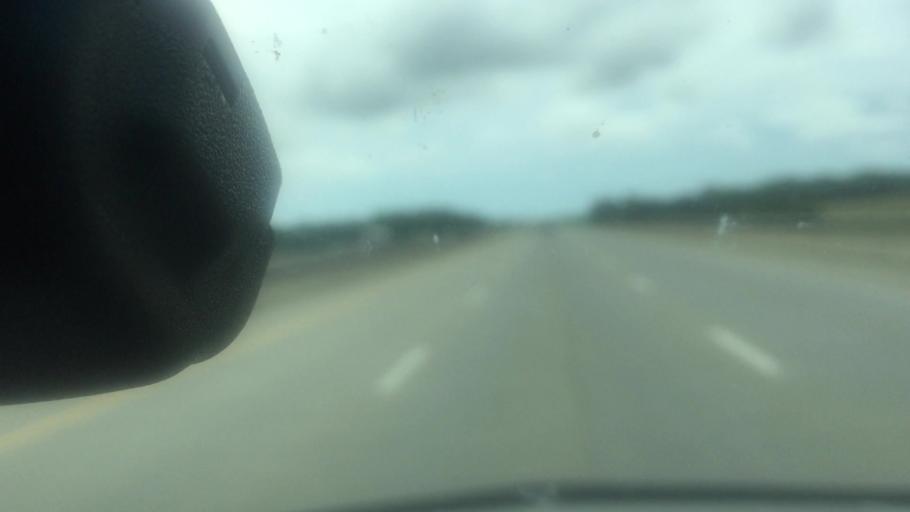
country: US
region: Illinois
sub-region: Logan County
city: Lincoln
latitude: 40.1289
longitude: -89.4171
